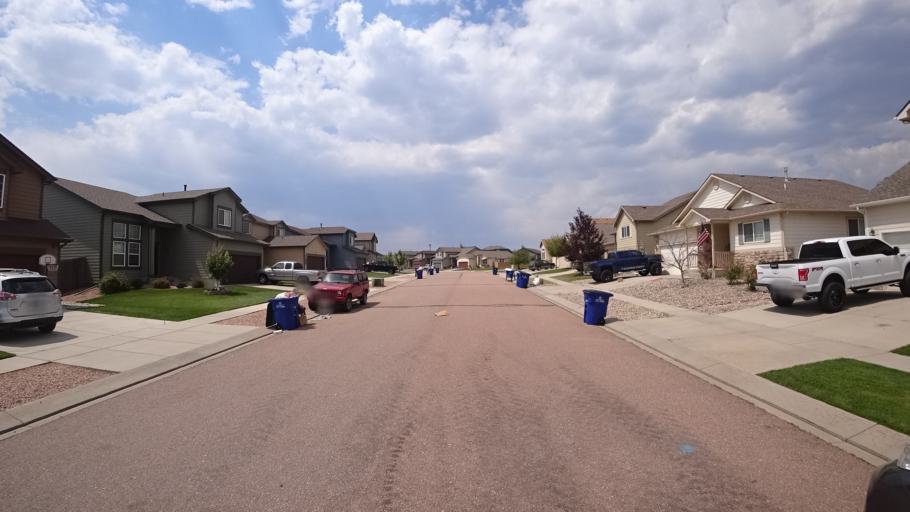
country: US
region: Colorado
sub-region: El Paso County
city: Black Forest
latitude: 38.9482
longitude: -104.6968
